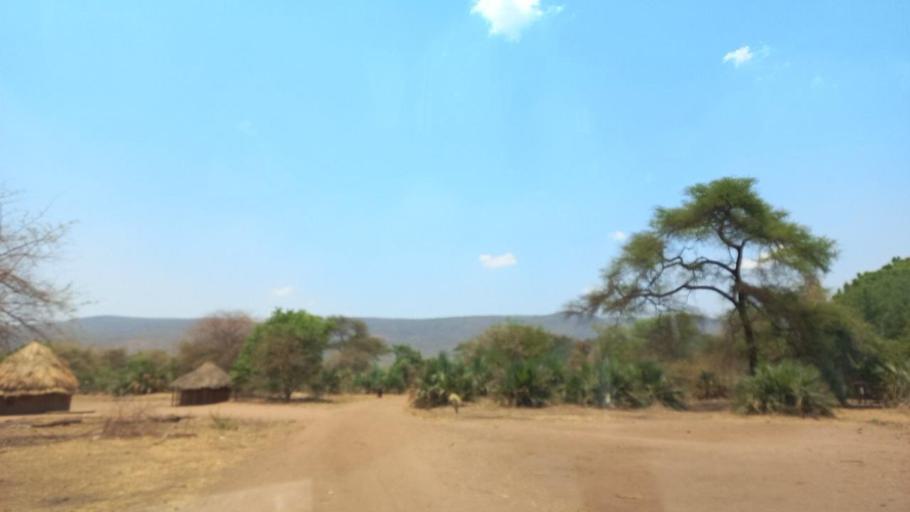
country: ZM
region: Lusaka
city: Luangwa
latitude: -15.1957
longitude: 30.1749
